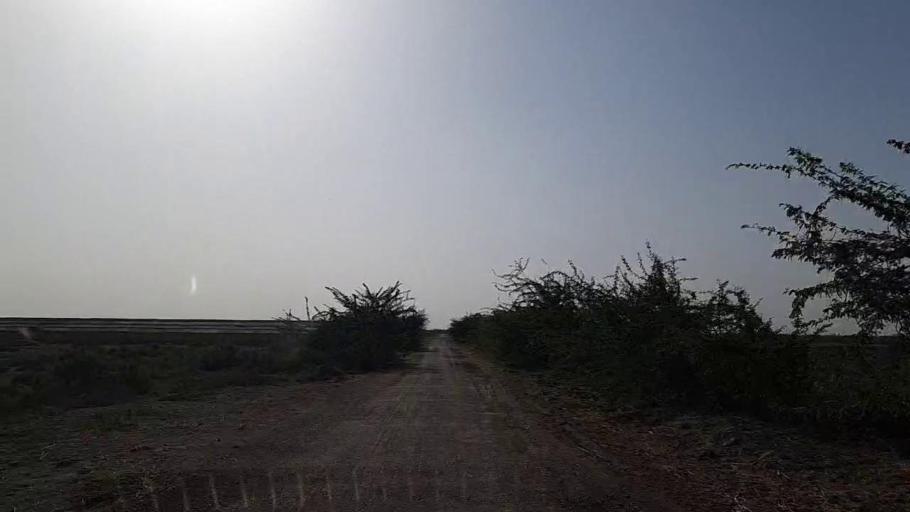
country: PK
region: Sindh
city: Jati
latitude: 24.2820
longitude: 68.2339
